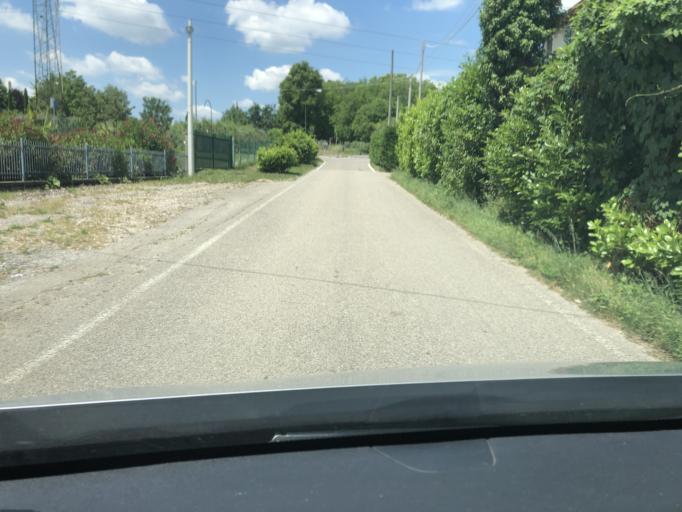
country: IT
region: Veneto
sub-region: Provincia di Verona
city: Rosegaferro
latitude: 45.3799
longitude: 10.8032
